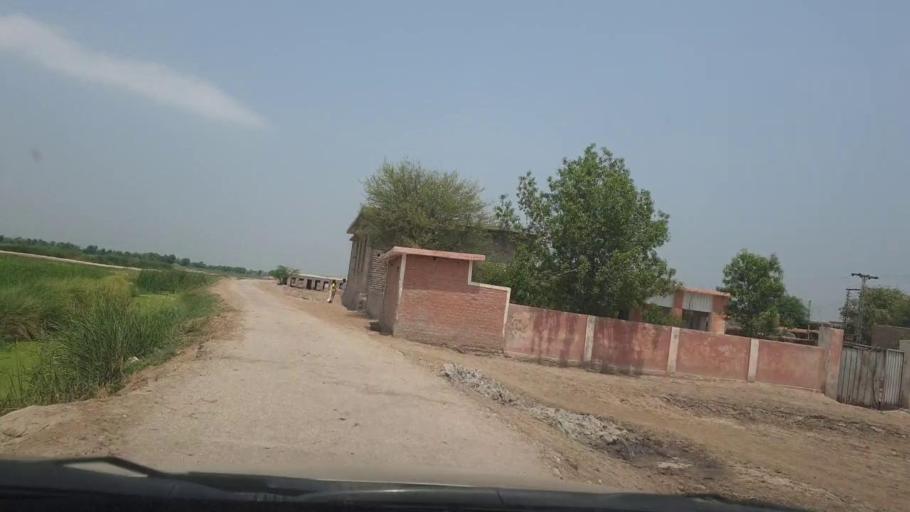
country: PK
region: Sindh
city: Ratodero
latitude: 27.7248
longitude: 68.2956
